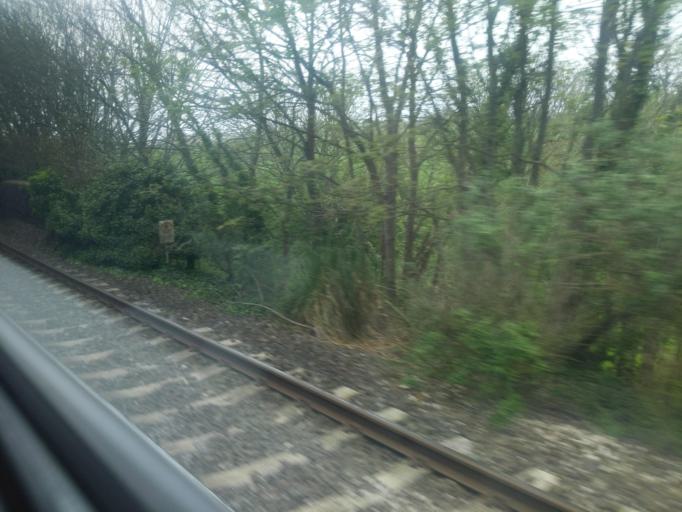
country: GB
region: England
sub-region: Cornwall
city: Hayle
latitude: 50.1733
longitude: -5.4352
